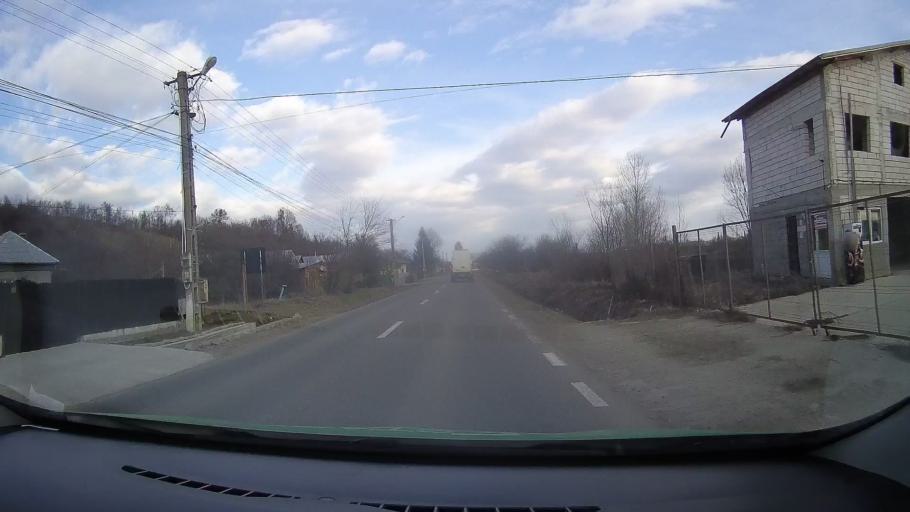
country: RO
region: Dambovita
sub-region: Comuna Gura Ocnitei
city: Gura Ocnitei
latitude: 44.9314
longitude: 25.5548
